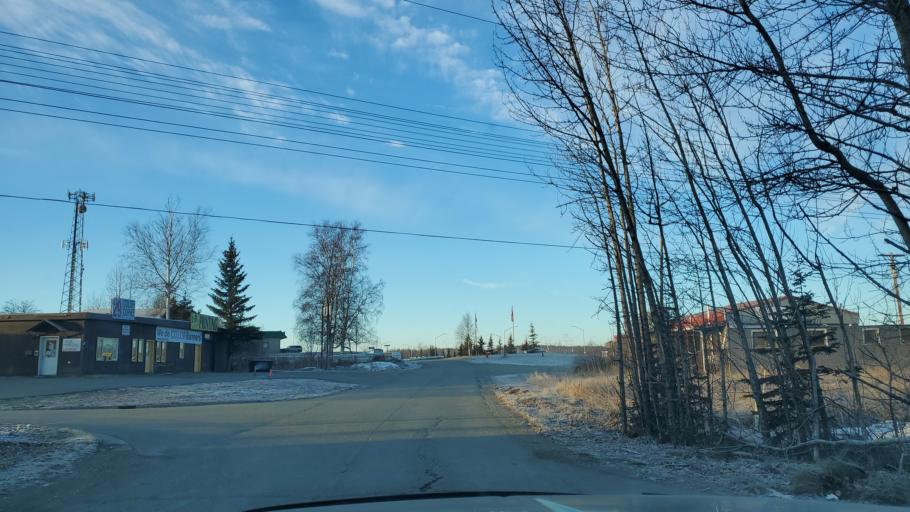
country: US
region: Alaska
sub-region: Matanuska-Susitna Borough
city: Wasilla
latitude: 61.5797
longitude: -149.4349
